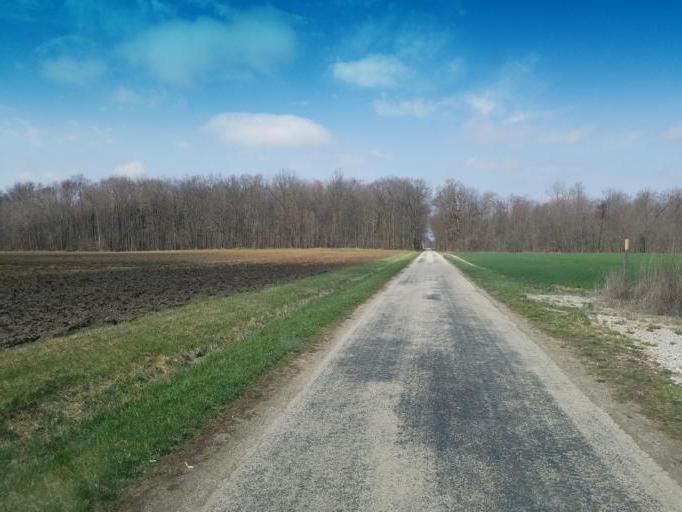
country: US
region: Ohio
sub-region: Crawford County
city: Bucyrus
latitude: 40.9356
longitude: -83.0814
